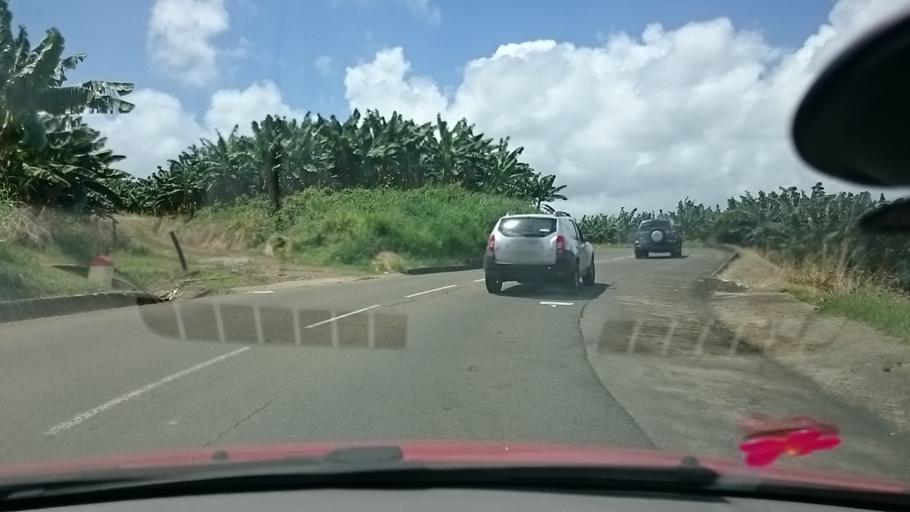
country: MQ
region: Martinique
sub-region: Martinique
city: Le Lamentin
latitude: 14.6250
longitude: -60.9703
